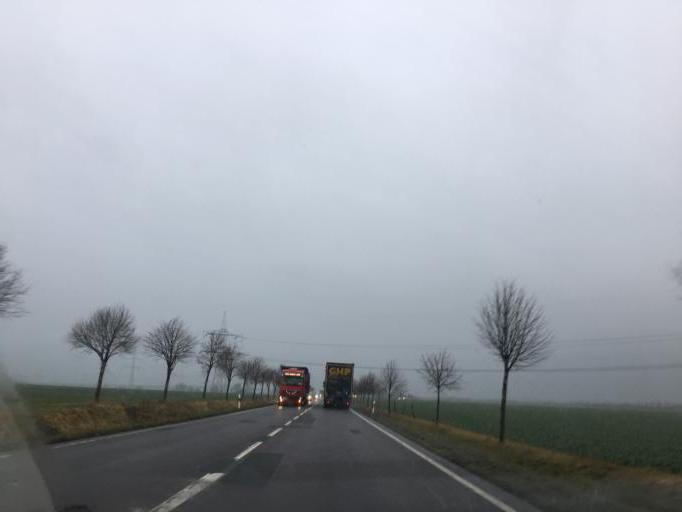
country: DE
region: Saxony-Anhalt
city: Gross Ammensleben
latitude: 52.2389
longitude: 11.5154
